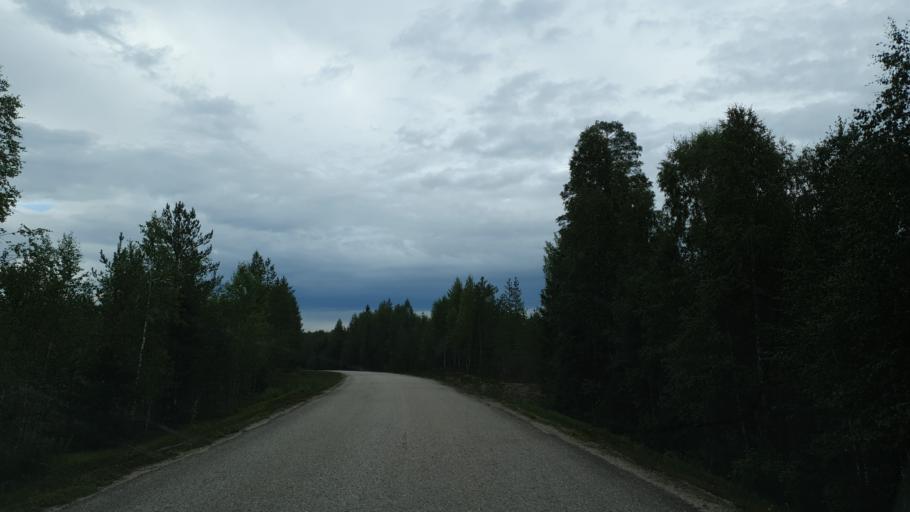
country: FI
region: Kainuu
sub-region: Kehys-Kainuu
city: Kuhmo
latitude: 64.3526
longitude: 29.1707
